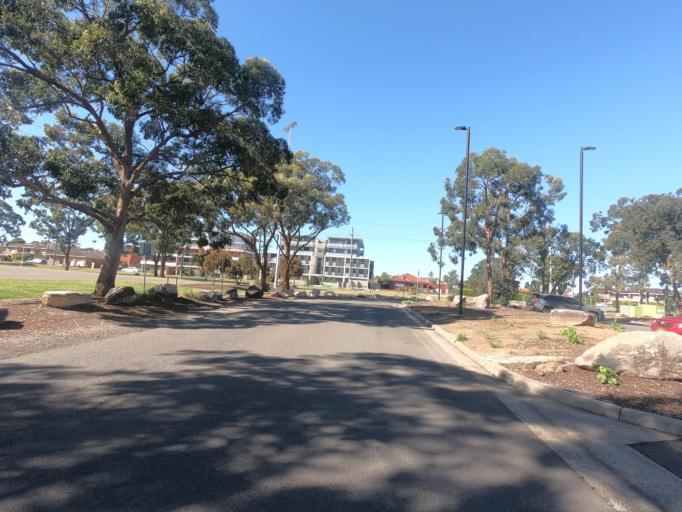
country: AU
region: New South Wales
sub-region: Liverpool
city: Miller
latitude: -33.9275
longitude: 150.9132
